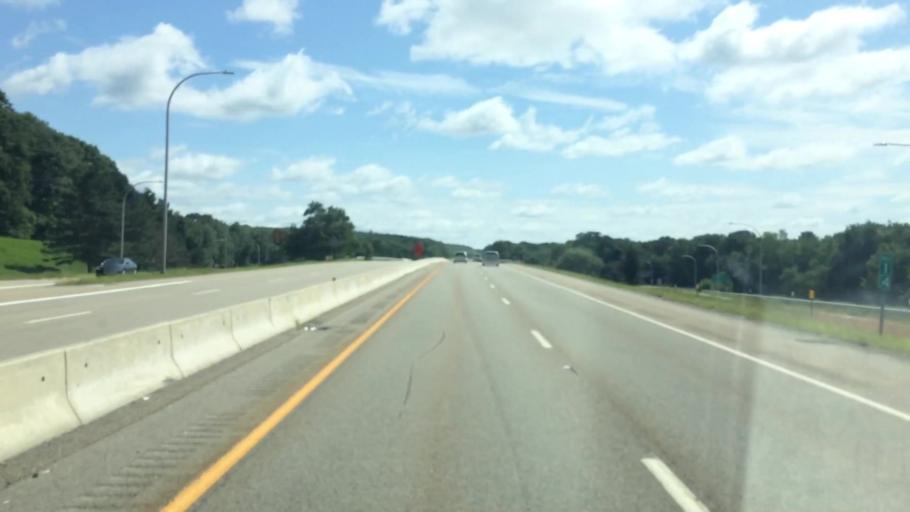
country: US
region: Rhode Island
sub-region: Providence County
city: Cumberland Hill
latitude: 41.9670
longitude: -71.4851
